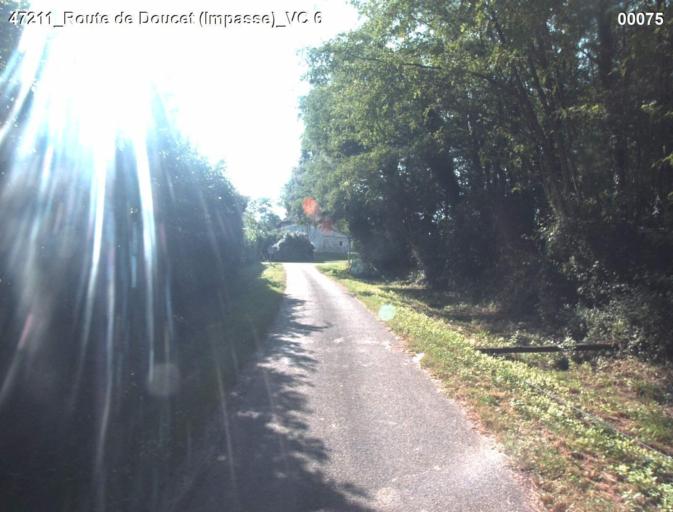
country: FR
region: Aquitaine
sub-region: Departement du Lot-et-Garonne
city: Mezin
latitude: 44.0209
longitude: 0.1977
